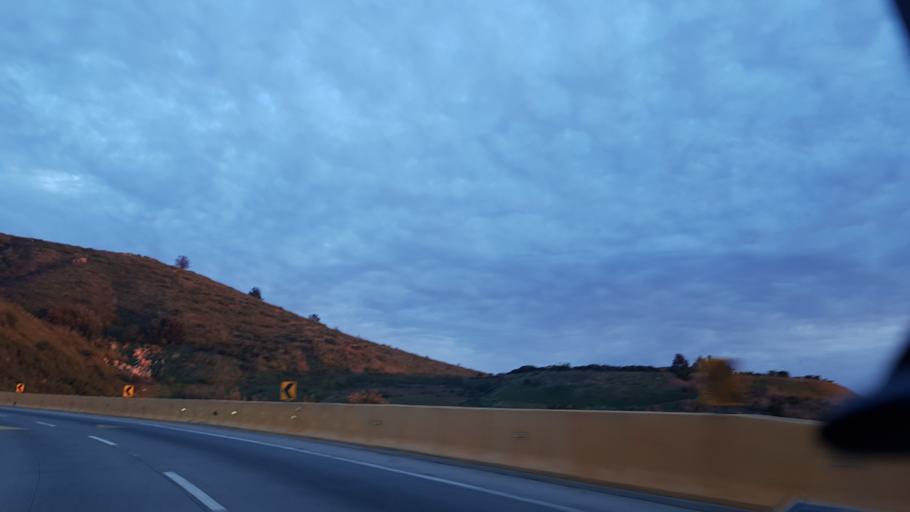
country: CL
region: Valparaiso
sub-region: Provincia de Valparaiso
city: Valparaiso
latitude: -33.0586
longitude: -71.6548
